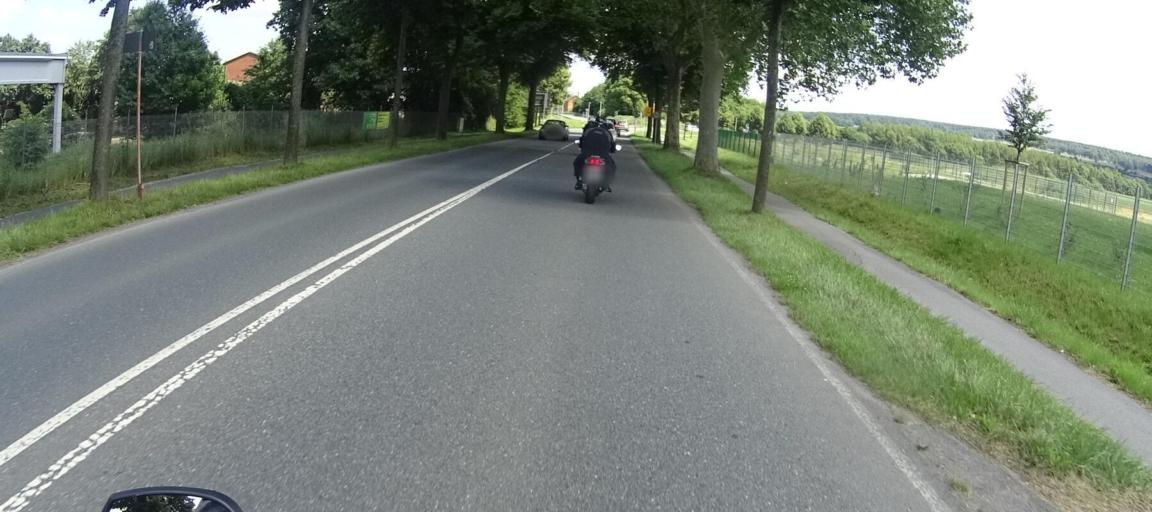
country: DE
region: Lower Saxony
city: Holzminden
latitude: 51.8395
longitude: 9.4697
